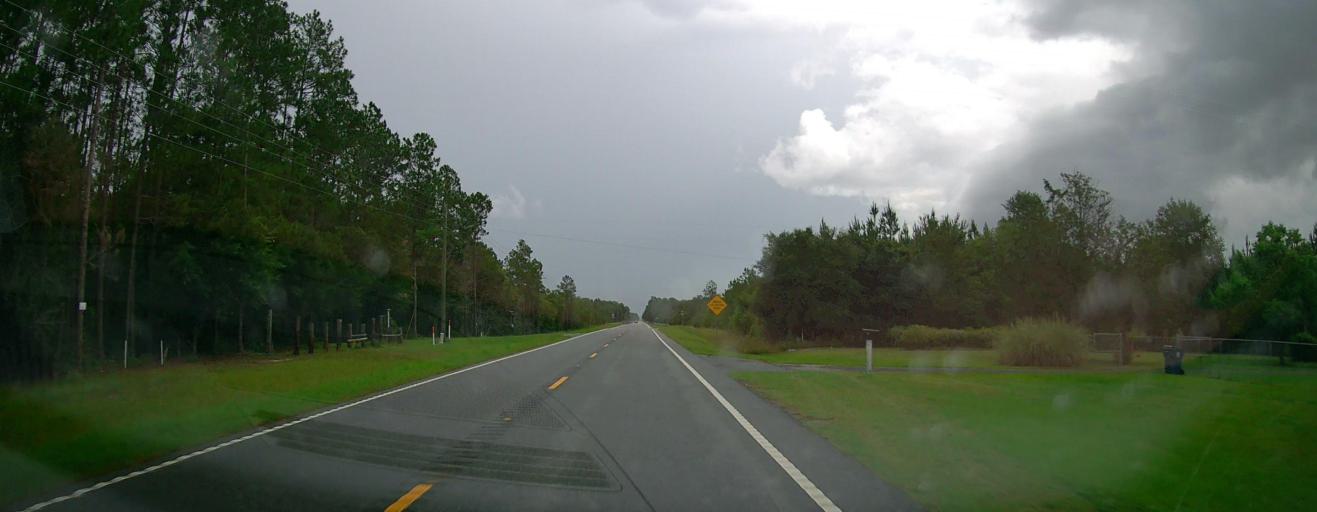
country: US
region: Georgia
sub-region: Brantley County
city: Nahunta
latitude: 31.3447
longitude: -82.0009
